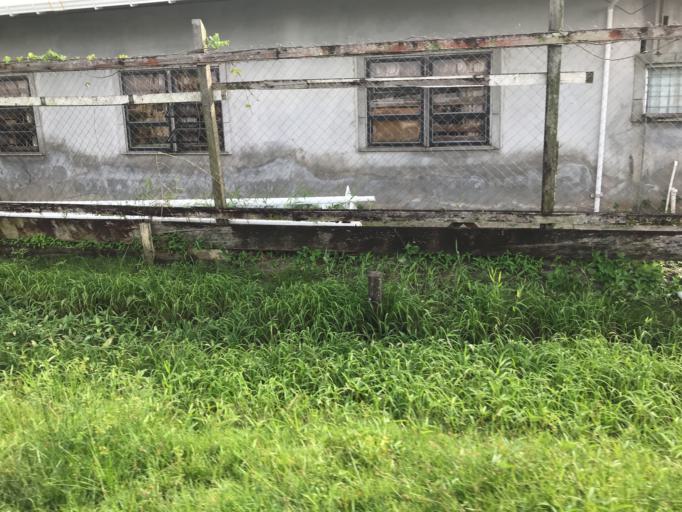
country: GY
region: Demerara-Mahaica
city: Georgetown
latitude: 6.8037
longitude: -58.1271
